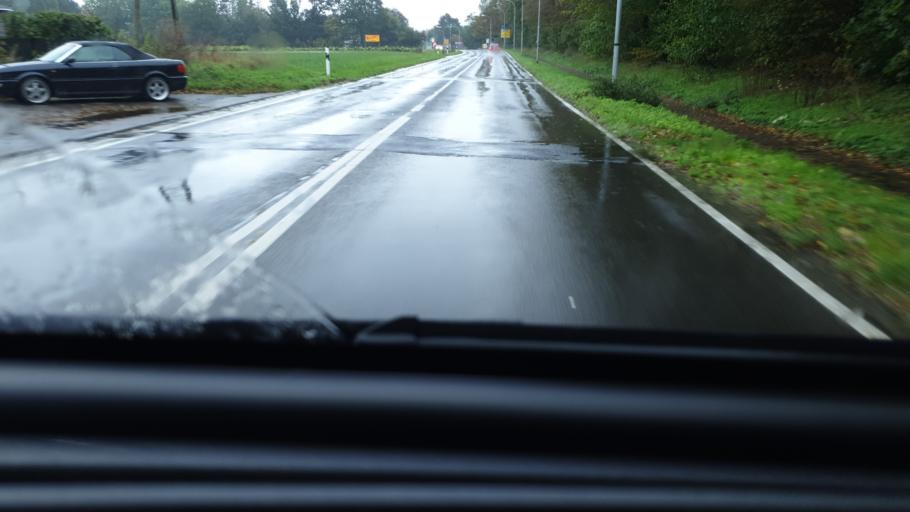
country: DE
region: North Rhine-Westphalia
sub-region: Regierungsbezirk Dusseldorf
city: Schwalmtal
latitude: 51.2097
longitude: 6.2945
